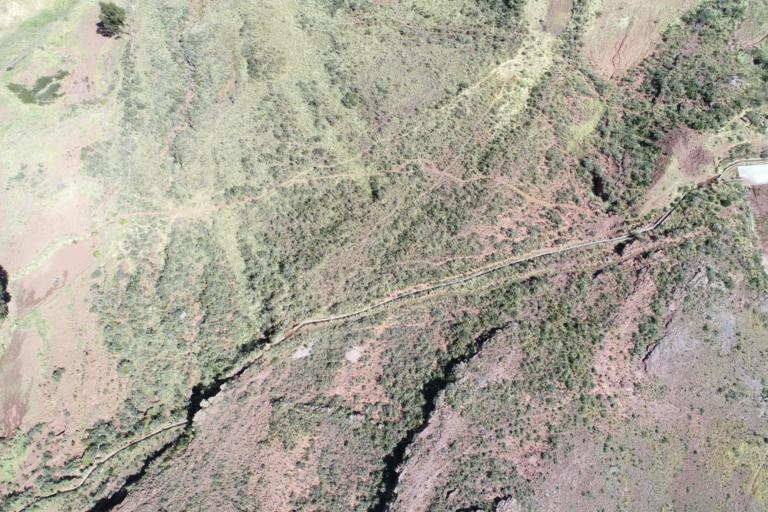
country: BO
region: La Paz
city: Tiahuanaco
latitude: -16.6109
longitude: -68.7649
